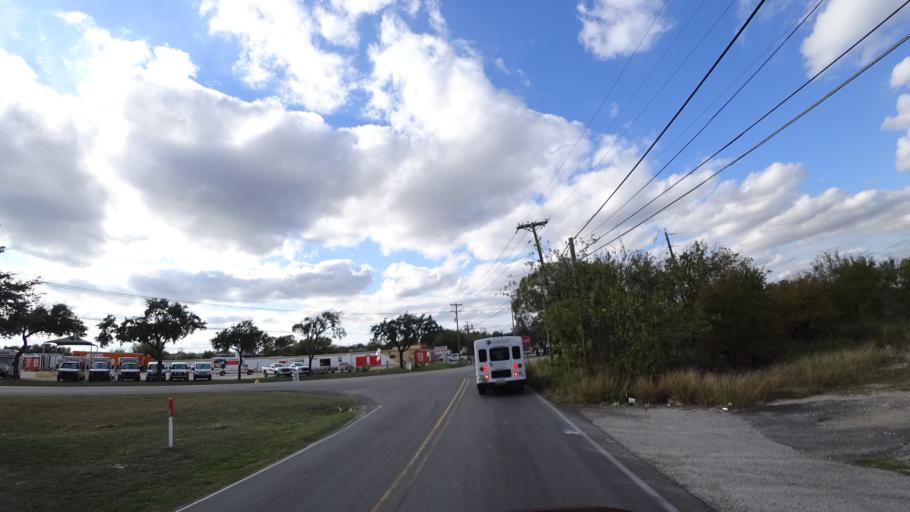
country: US
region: Texas
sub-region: Travis County
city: Windemere
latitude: 30.4517
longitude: -97.6620
